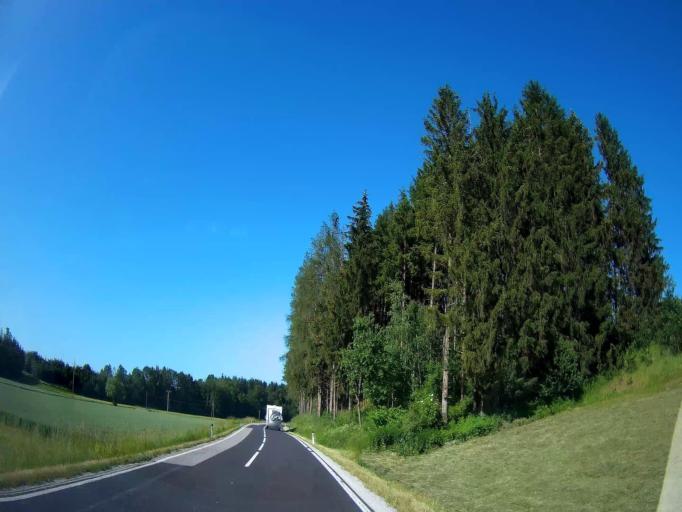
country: AT
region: Upper Austria
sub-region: Politischer Bezirk Braunau am Inn
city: Braunau am Inn
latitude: 48.1523
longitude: 13.0361
